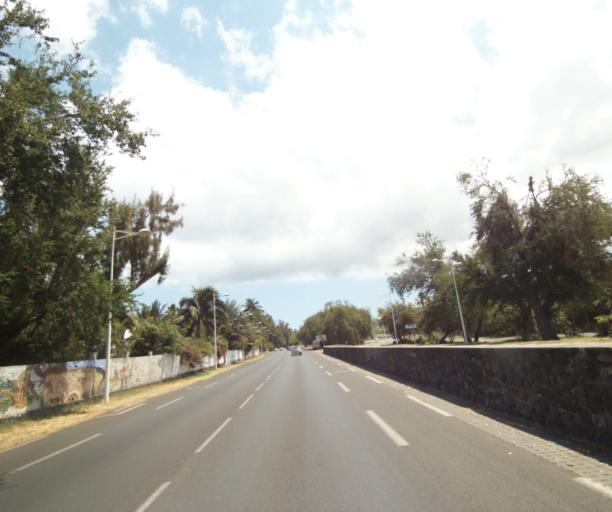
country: RE
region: Reunion
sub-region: Reunion
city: Trois-Bassins
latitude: -21.0773
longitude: 55.2283
